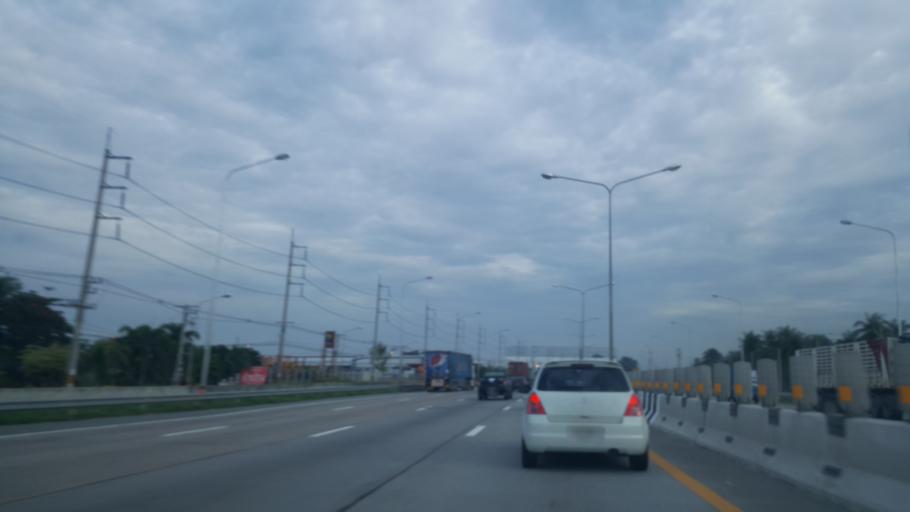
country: TH
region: Chon Buri
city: Si Racha
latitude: 13.2209
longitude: 101.0045
